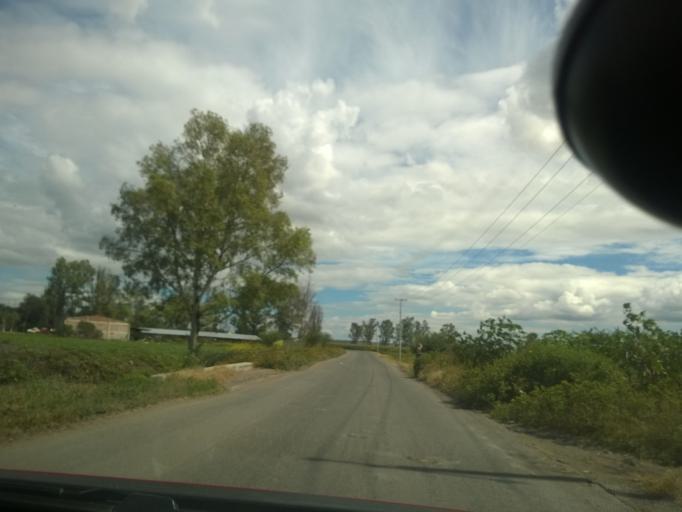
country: MX
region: Guanajuato
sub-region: Leon
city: Plan Guanajuato (La Sandia)
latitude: 20.9623
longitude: -101.6499
